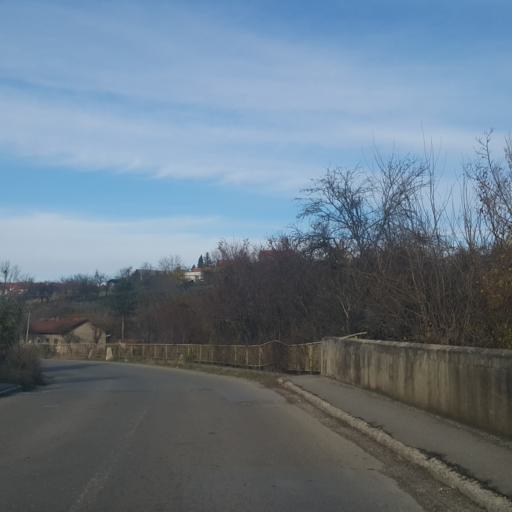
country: RS
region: Central Serbia
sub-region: Belgrade
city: Lazarevac
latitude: 44.3750
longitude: 20.4078
